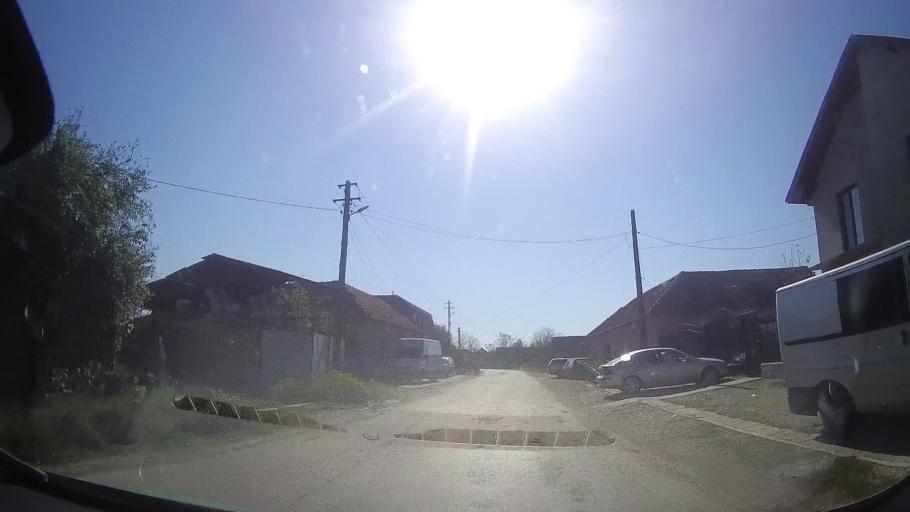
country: RO
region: Timis
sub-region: Comuna Bethausen
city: Bethausen
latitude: 45.8679
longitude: 21.9667
